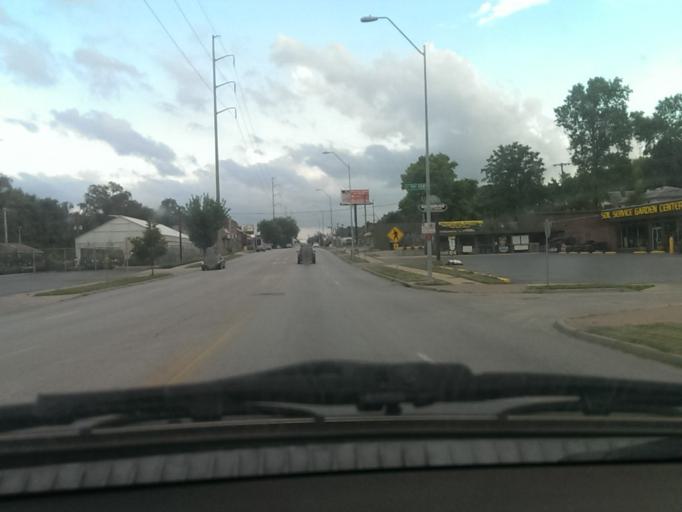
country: US
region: Kansas
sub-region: Johnson County
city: Mission Hills
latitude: 38.9982
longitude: -94.5754
